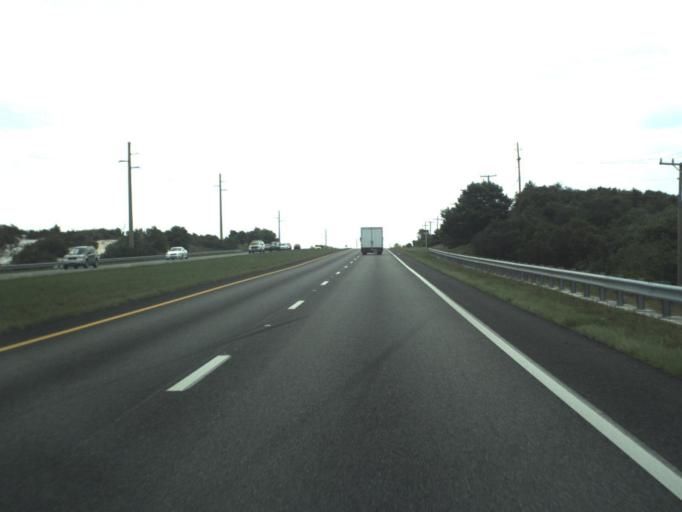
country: US
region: Florida
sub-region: Martin County
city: Hobe Sound
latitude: 27.0191
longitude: -80.1065
